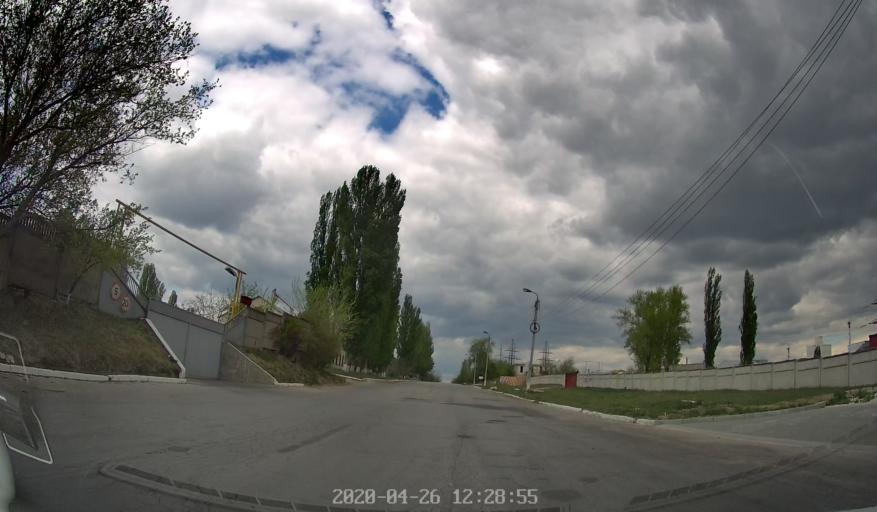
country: MD
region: Chisinau
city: Chisinau
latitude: 46.9997
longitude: 28.9059
